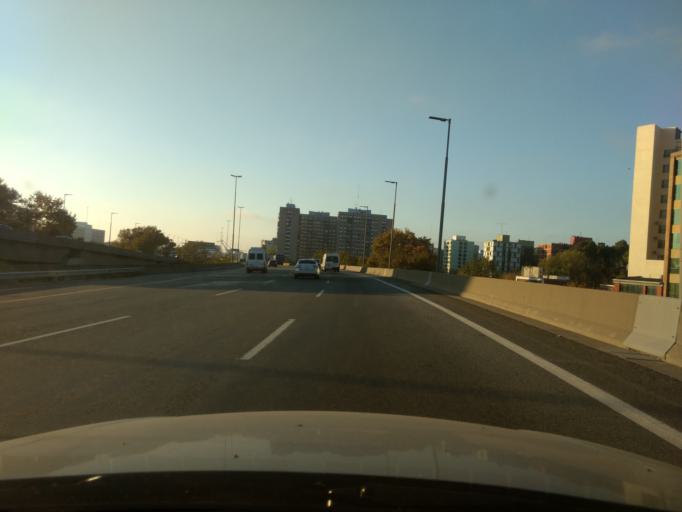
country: AR
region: Buenos Aires F.D.
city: Buenos Aires
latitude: -34.6239
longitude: -58.3646
